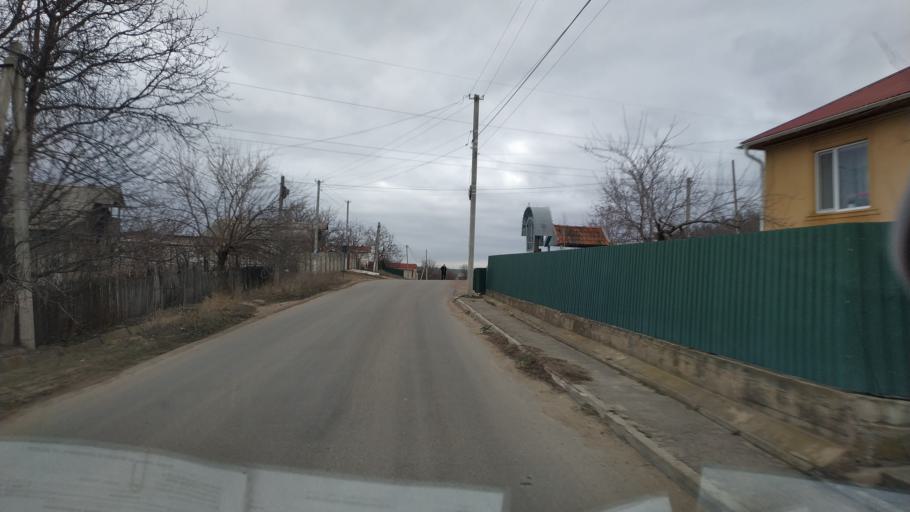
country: MD
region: Causeni
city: Causeni
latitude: 46.6580
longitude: 29.4454
